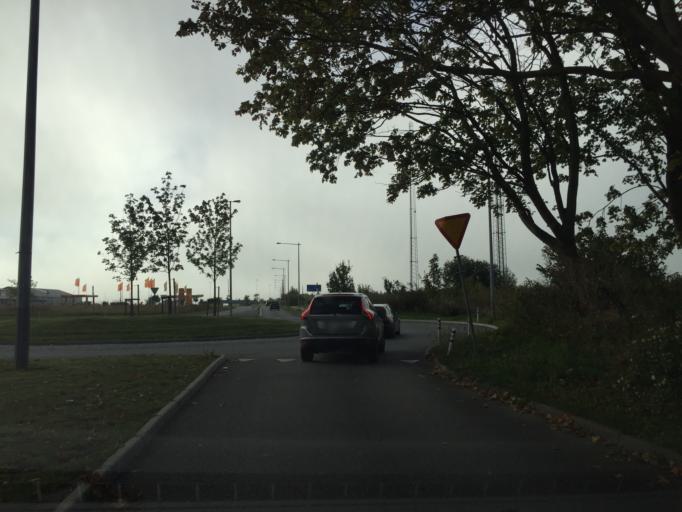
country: SE
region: Skane
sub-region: Staffanstorps Kommun
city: Staffanstorp
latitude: 55.6319
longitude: 13.1859
